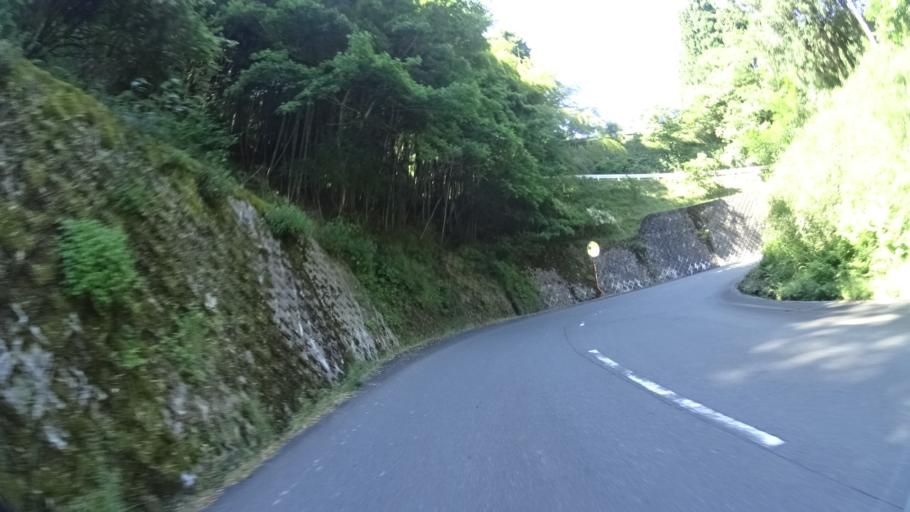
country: JP
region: Kyoto
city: Fukuchiyama
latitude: 35.3715
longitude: 135.0552
